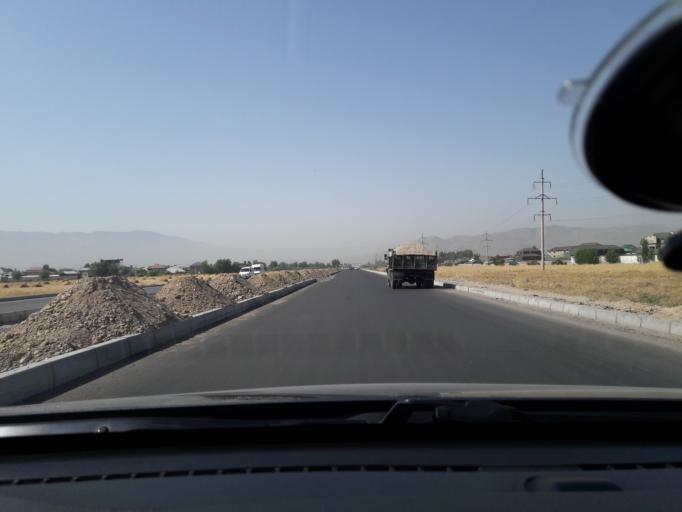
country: TJ
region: Dushanbe
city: Dushanbe
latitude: 38.4967
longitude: 68.7544
